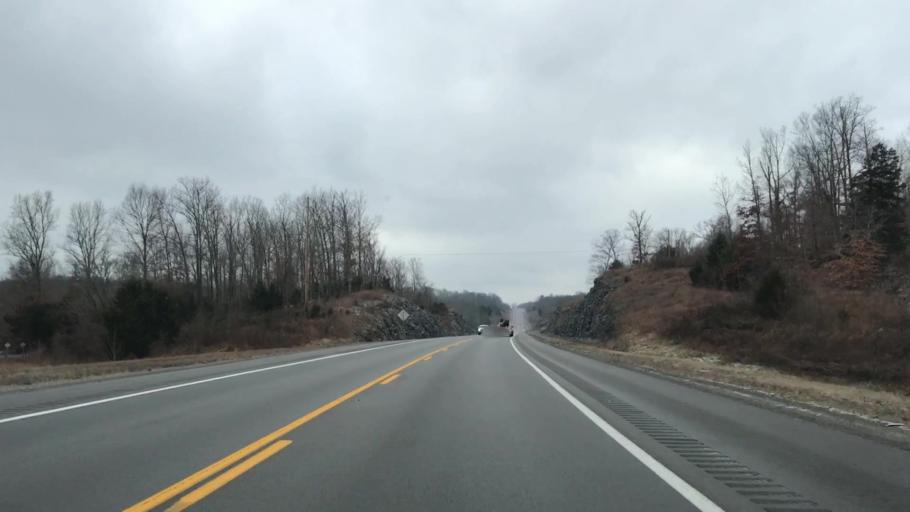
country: US
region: Kentucky
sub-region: Adair County
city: Columbia
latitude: 37.0360
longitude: -85.3752
